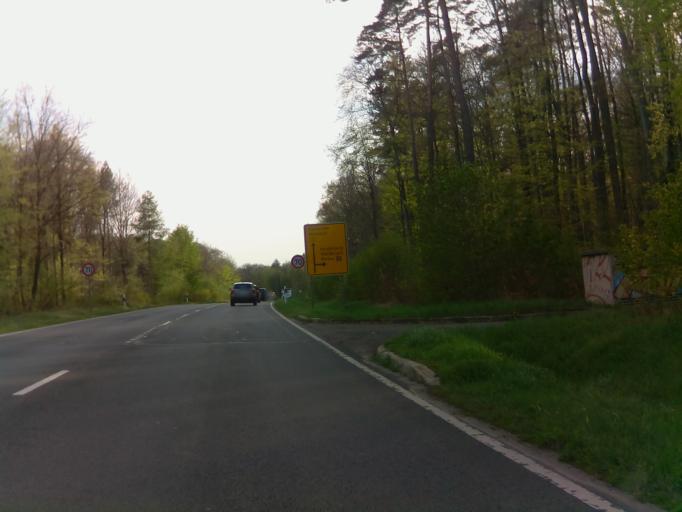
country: DE
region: Baden-Wuerttemberg
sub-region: Karlsruhe Region
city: Limbach
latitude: 49.4956
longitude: 9.2655
